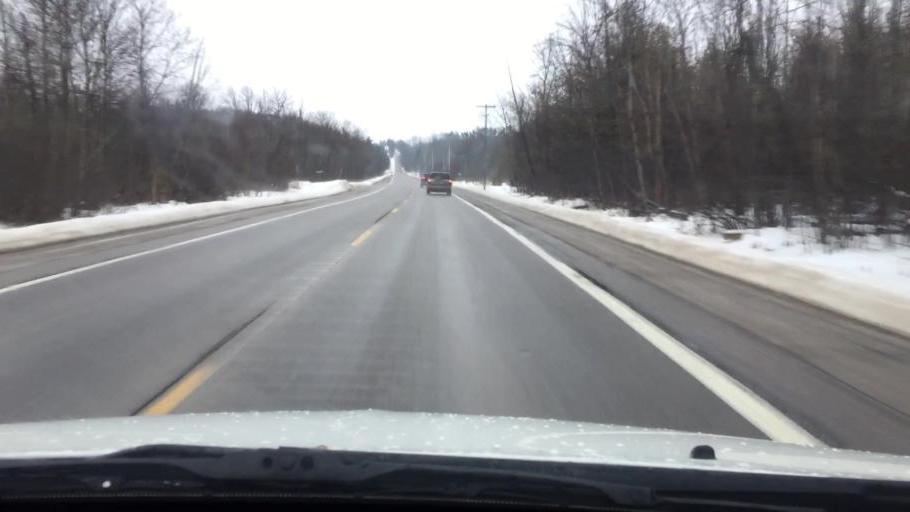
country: US
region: Michigan
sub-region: Charlevoix County
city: East Jordan
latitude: 45.2355
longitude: -85.1816
